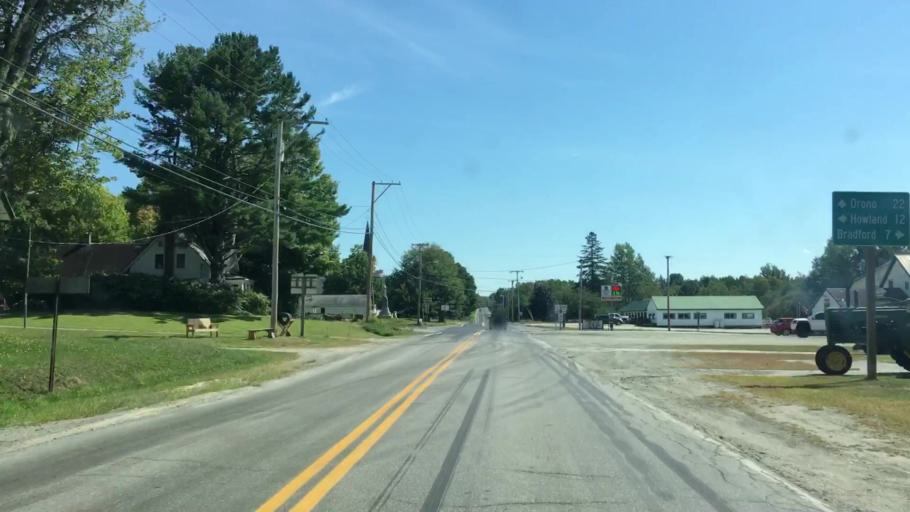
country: US
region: Maine
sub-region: Penobscot County
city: Bradford
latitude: 45.1674
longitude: -68.8455
